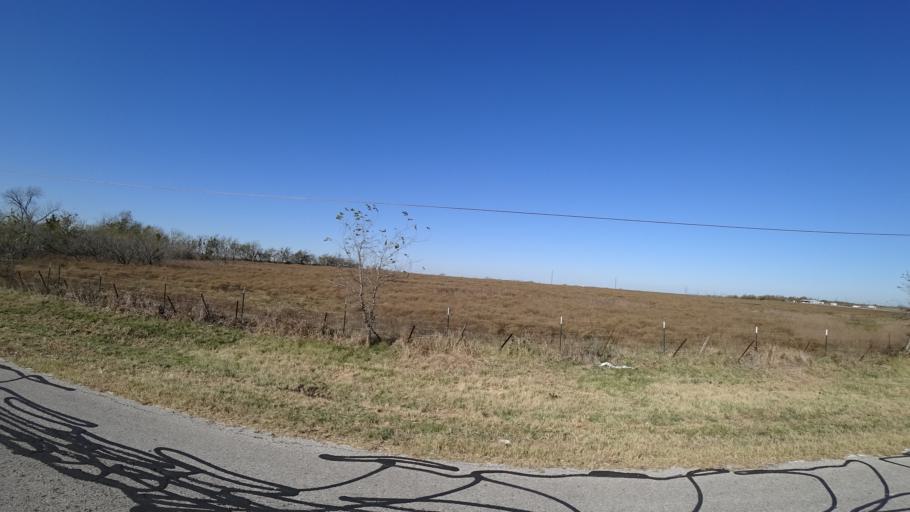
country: US
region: Texas
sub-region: Travis County
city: Garfield
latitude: 30.1096
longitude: -97.6511
